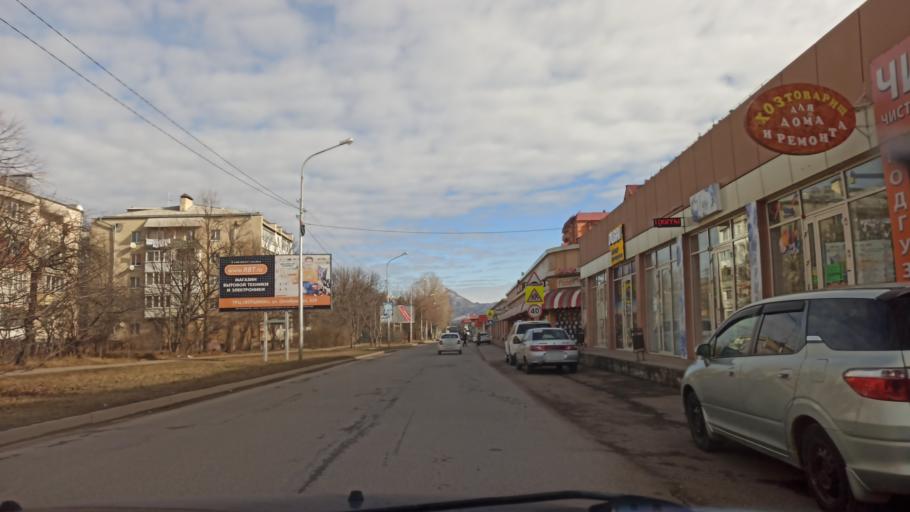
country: RU
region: Stavropol'skiy
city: Yessentukskaya
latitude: 44.0449
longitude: 42.8916
